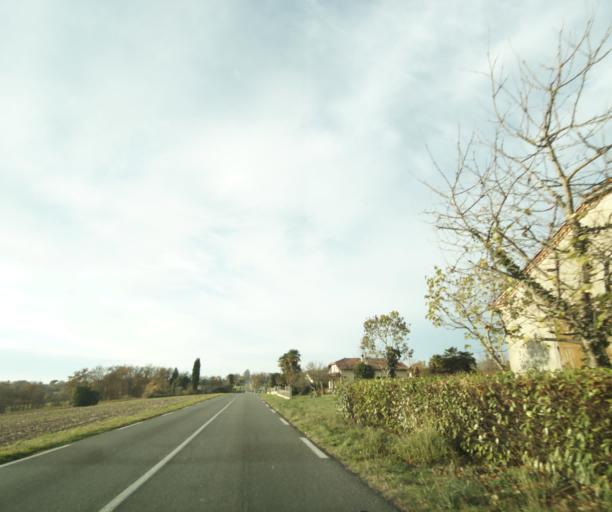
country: FR
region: Midi-Pyrenees
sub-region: Departement du Gers
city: Cazaubon
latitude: 43.9306
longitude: -0.0497
